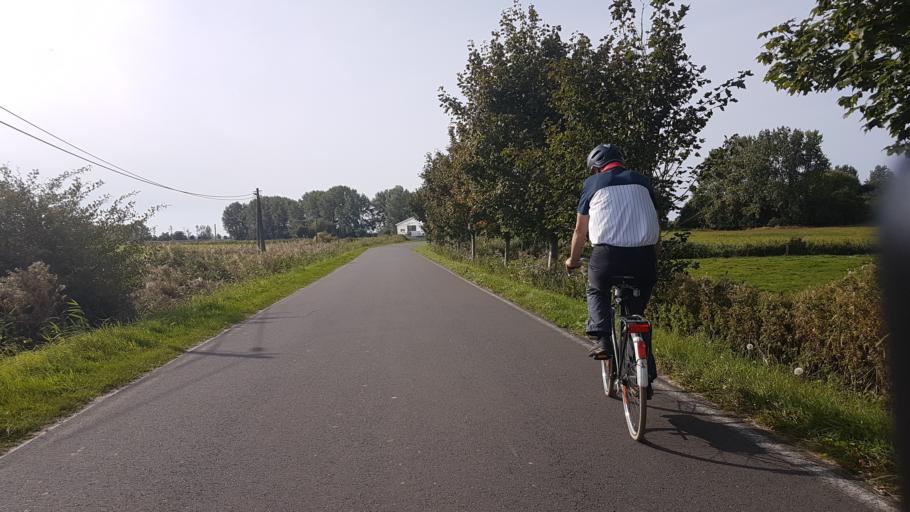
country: DE
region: Mecklenburg-Vorpommern
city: Gingst
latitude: 54.4506
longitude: 13.1487
